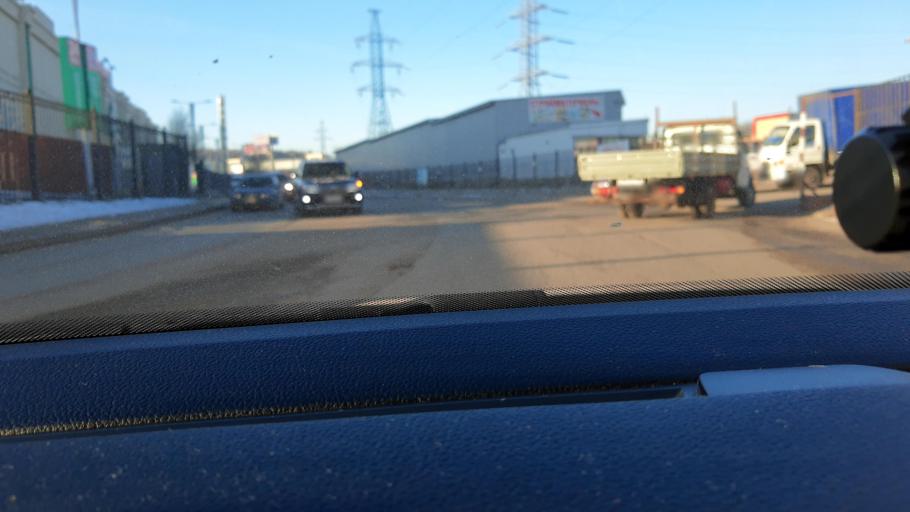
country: RU
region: Moscow
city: Vatutino
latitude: 55.8994
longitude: 37.6765
